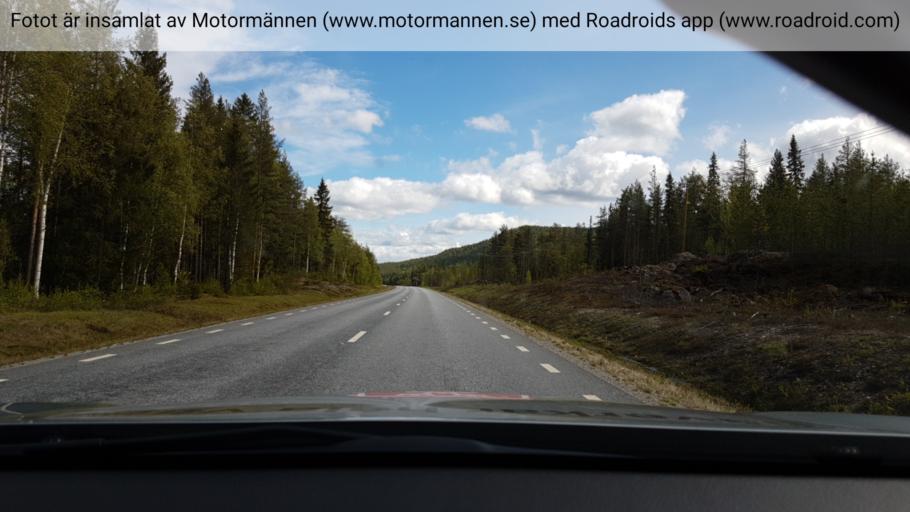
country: SE
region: Vaesterbotten
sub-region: Asele Kommun
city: Insjon
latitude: 64.1792
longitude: 17.7895
